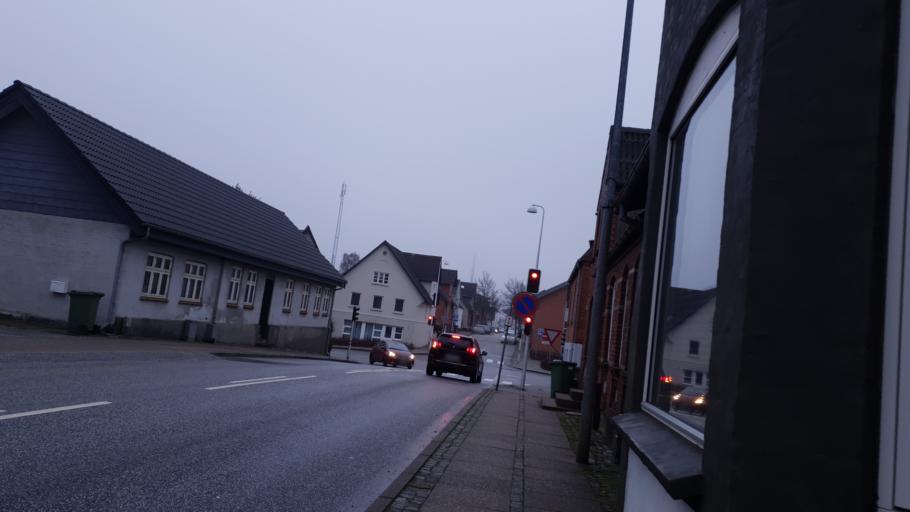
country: DK
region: Central Jutland
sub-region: Hedensted Kommune
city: Hedensted
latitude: 55.7712
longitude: 9.6982
